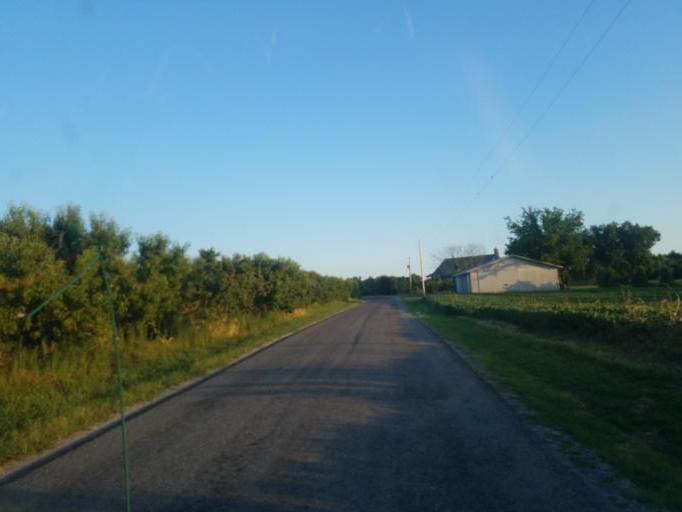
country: US
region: Illinois
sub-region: Jackson County
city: Murphysboro
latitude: 37.6791
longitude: -89.3131
